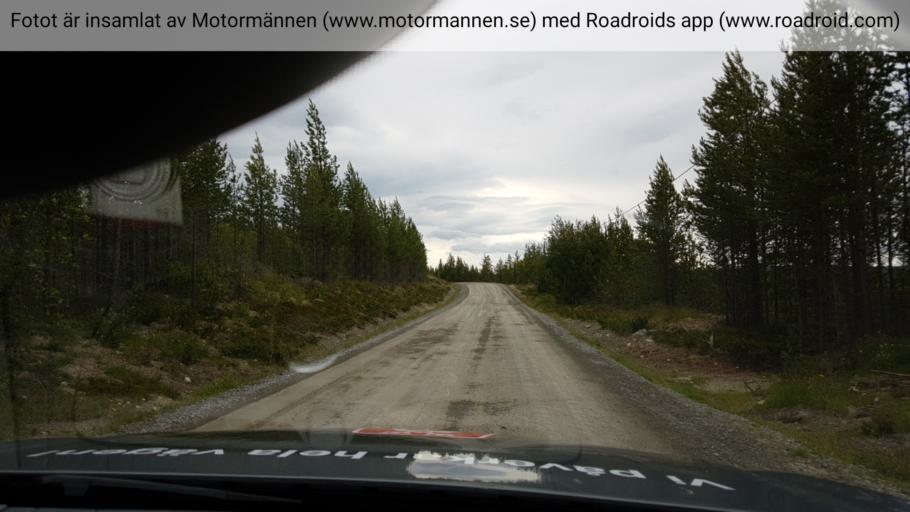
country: SE
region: Jaemtland
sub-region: Bergs Kommun
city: Hoverberg
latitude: 62.7759
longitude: 13.8271
